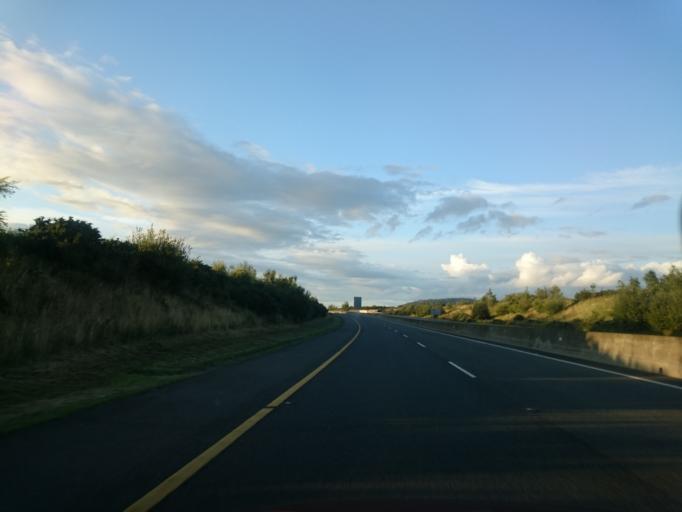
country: IE
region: Leinster
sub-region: Loch Garman
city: Gorey
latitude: 52.6696
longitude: -6.2606
